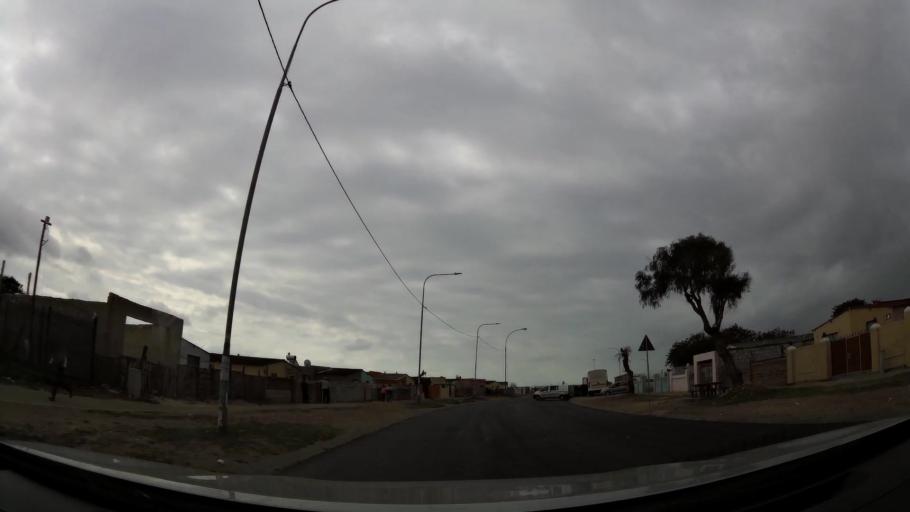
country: ZA
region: Eastern Cape
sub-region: Nelson Mandela Bay Metropolitan Municipality
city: Port Elizabeth
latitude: -33.8918
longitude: 25.5935
